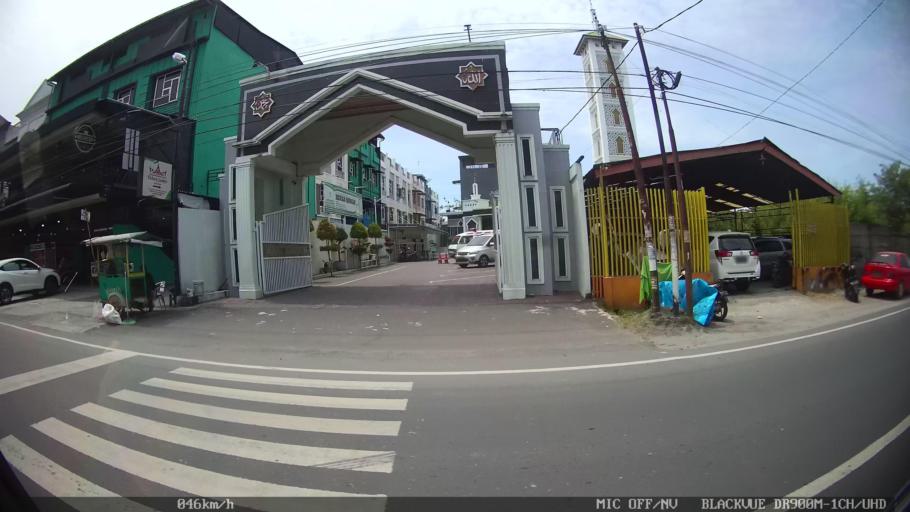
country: ID
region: North Sumatra
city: Sunggal
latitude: 3.5765
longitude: 98.6194
